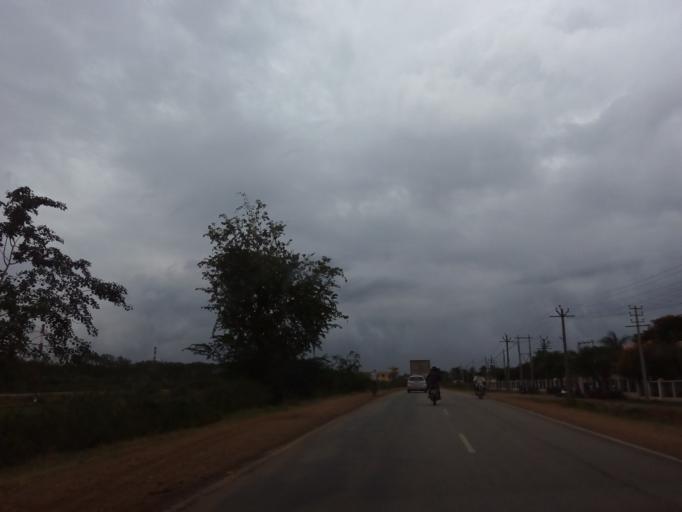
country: IN
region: Karnataka
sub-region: Davanagere
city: Harihar
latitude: 14.5297
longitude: 75.7746
